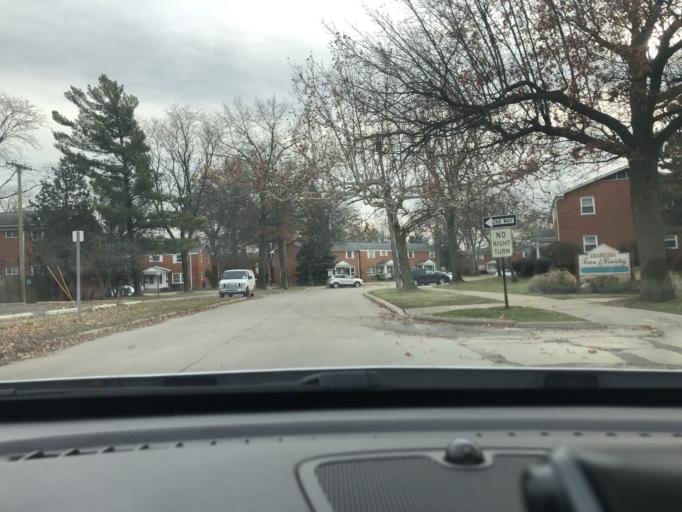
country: US
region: Michigan
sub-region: Wayne County
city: Dearborn Heights
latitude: 42.3413
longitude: -83.2397
